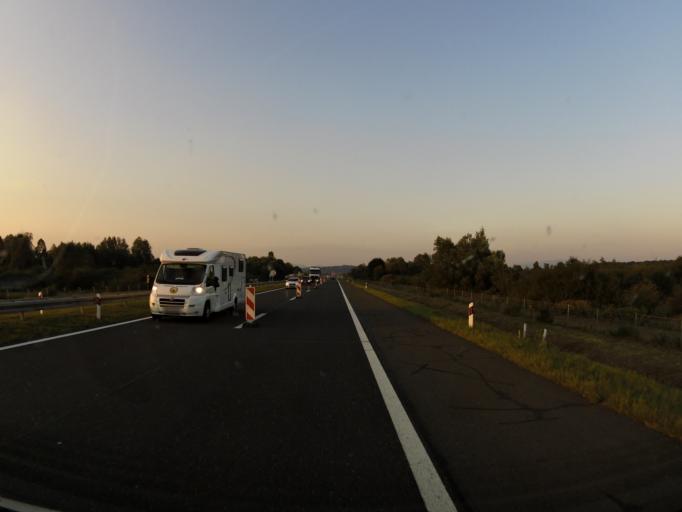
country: HR
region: Zagrebacka
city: Jakovlje
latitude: 45.9838
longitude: 15.8577
